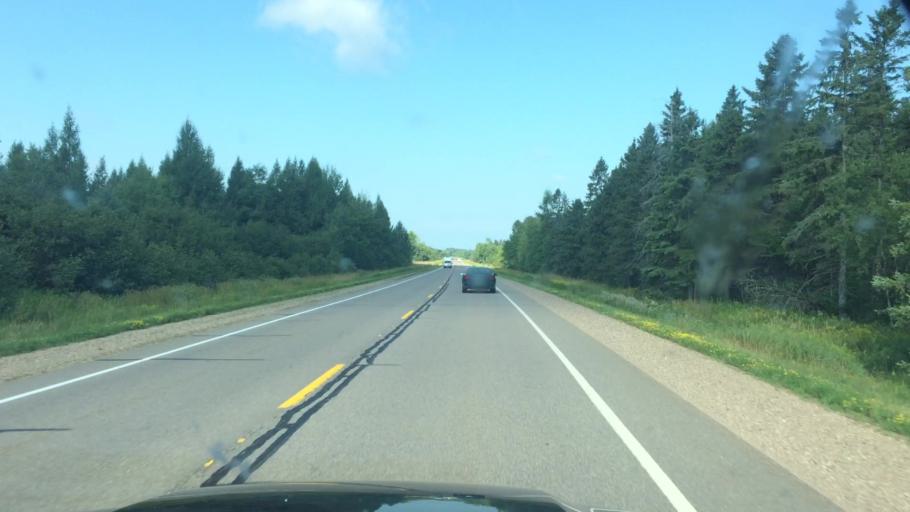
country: US
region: Wisconsin
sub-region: Langlade County
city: Antigo
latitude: 45.1458
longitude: -89.3230
